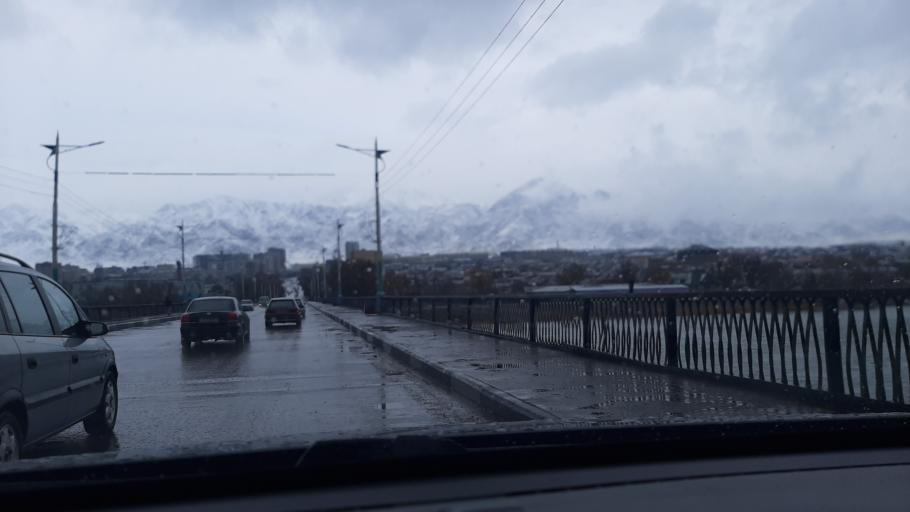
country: TJ
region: Viloyati Sughd
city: Khujand
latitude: 40.2896
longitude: 69.6208
